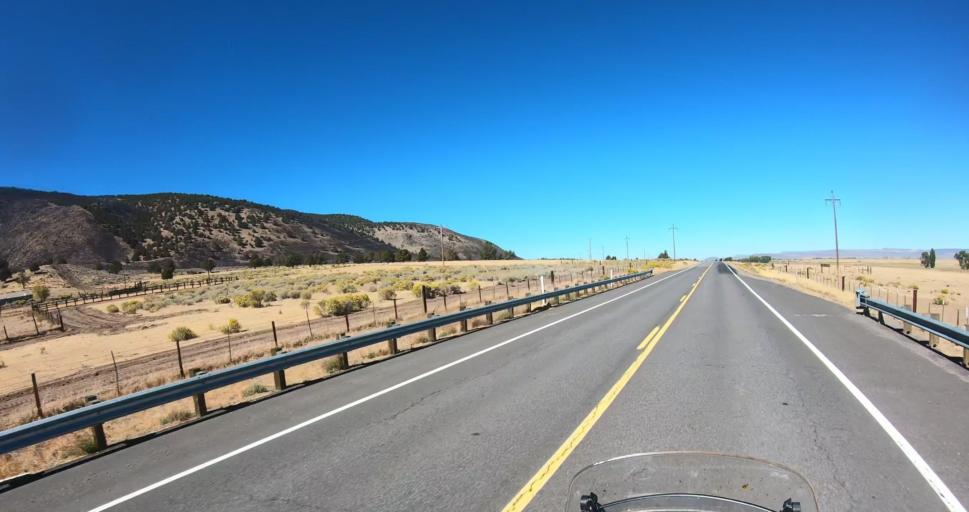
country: US
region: Oregon
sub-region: Lake County
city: Lakeview
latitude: 42.6447
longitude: -120.5207
